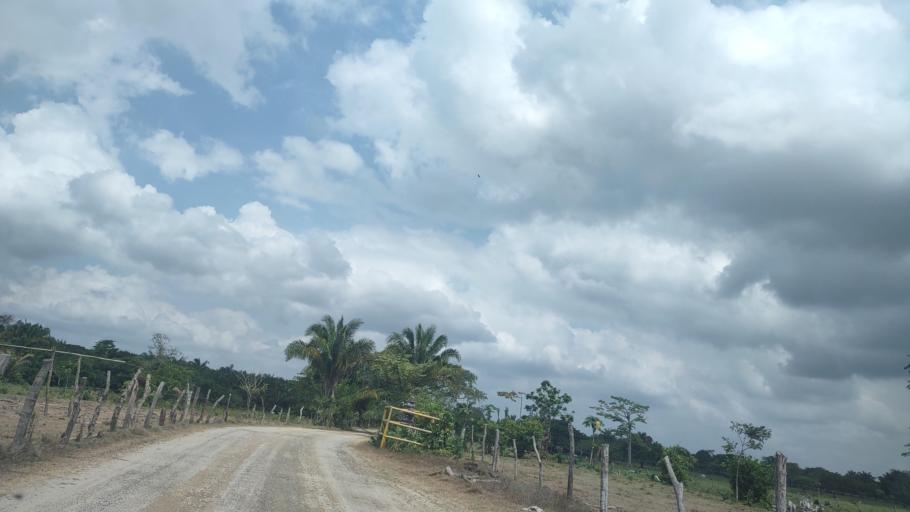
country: MX
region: Veracruz
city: Las Choapas
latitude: 17.9618
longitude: -94.1223
